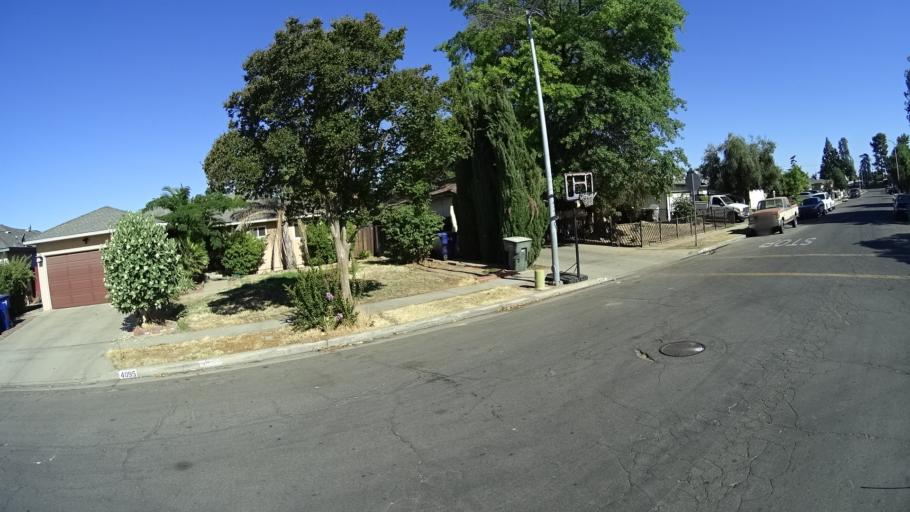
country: US
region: California
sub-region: Fresno County
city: Fresno
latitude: 36.7918
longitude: -119.8403
